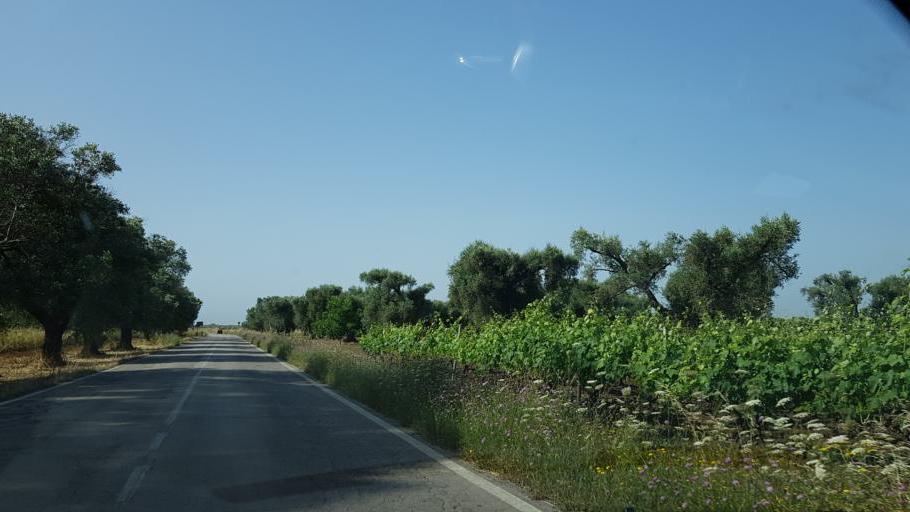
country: IT
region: Apulia
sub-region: Provincia di Brindisi
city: Mesagne
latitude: 40.5323
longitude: 17.8193
